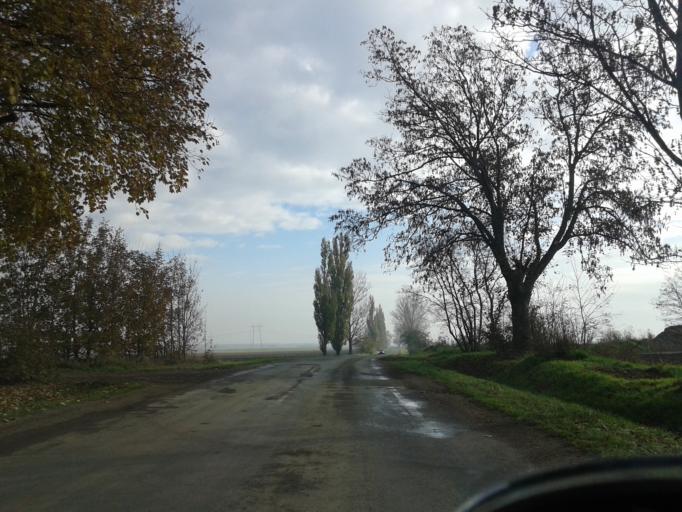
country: HU
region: Fejer
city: Pusztaszabolcs
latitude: 47.1358
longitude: 18.7816
